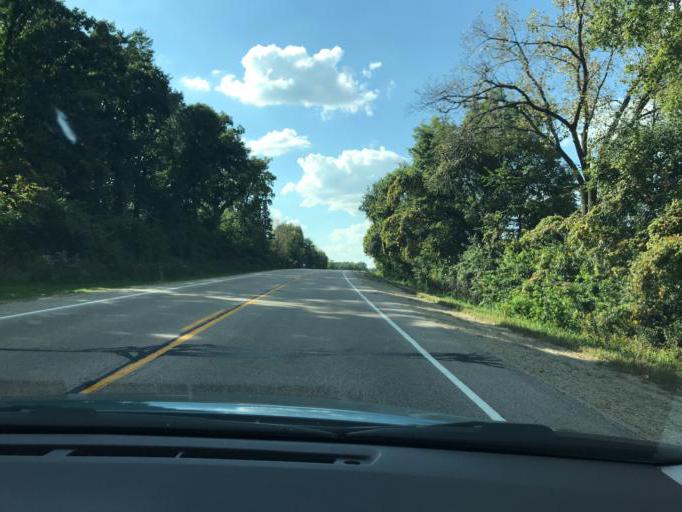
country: US
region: Wisconsin
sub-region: Rock County
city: Orfordville
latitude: 42.5263
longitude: -89.2232
